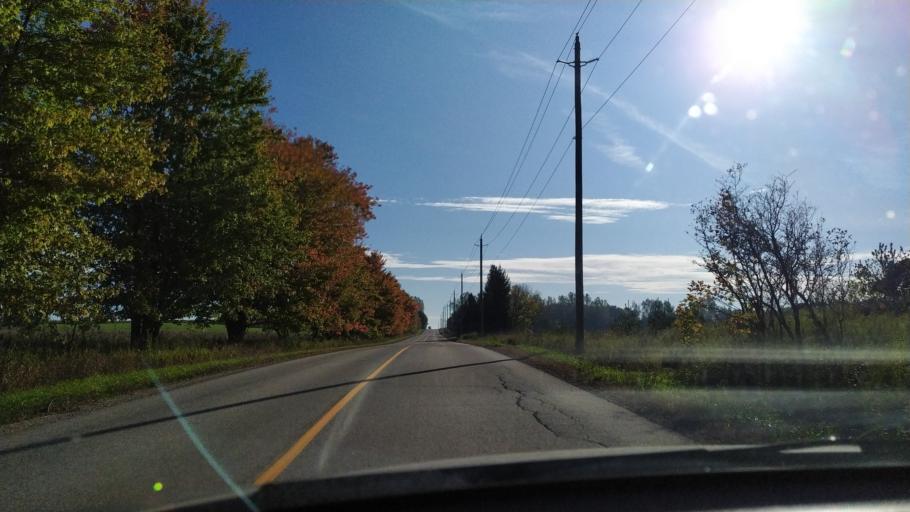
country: CA
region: Ontario
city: Stratford
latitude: 43.4955
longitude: -80.7579
